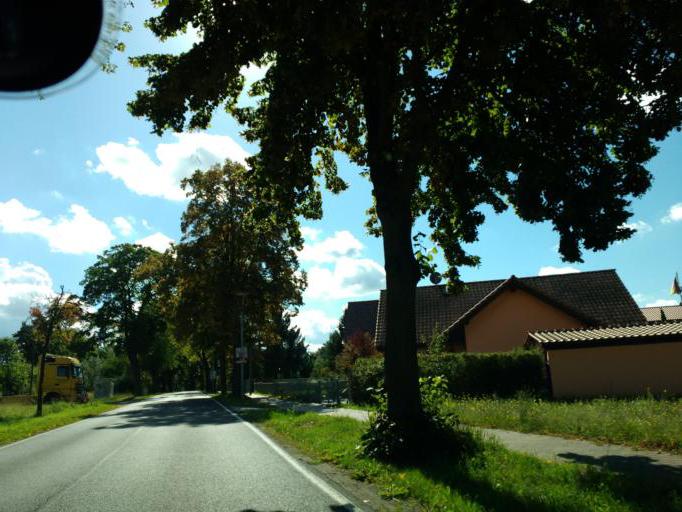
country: DE
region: Brandenburg
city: Mittenwalde
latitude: 52.2391
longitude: 13.5652
